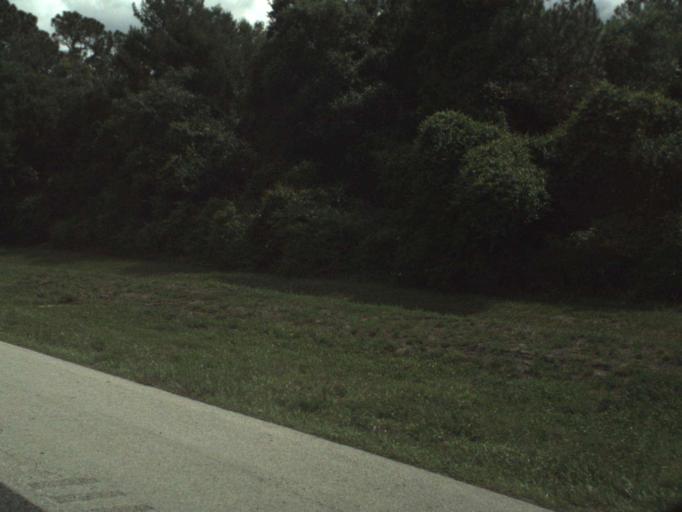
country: US
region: Florida
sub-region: Volusia County
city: Lake Helen
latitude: 28.9998
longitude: -81.2433
